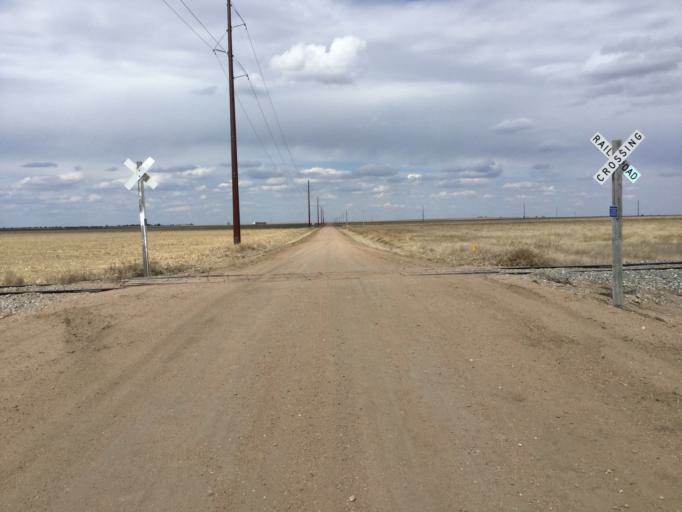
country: US
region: Kansas
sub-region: Grant County
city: Ulysses
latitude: 37.5666
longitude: -101.4353
